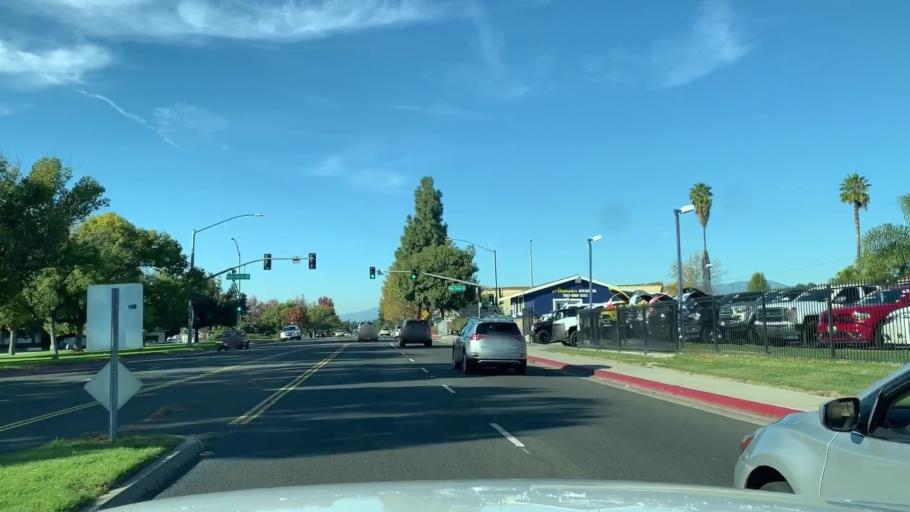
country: US
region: California
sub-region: Los Angeles County
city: South Whittier
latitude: 33.9728
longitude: -118.0450
